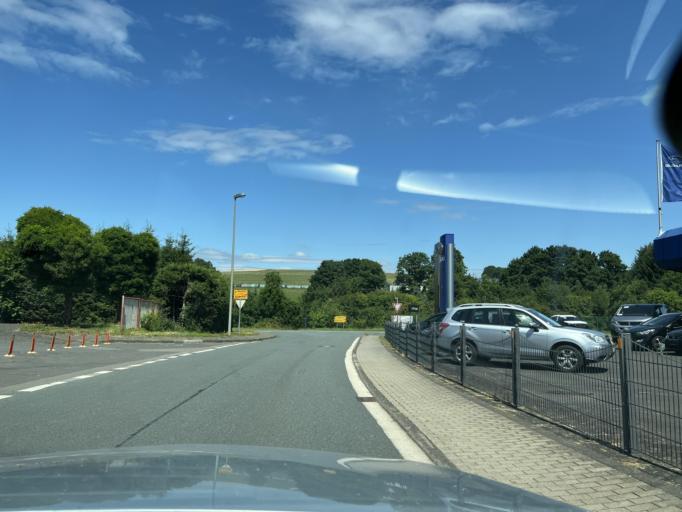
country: DE
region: North Rhine-Westphalia
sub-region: Regierungsbezirk Arnsberg
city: Wenden
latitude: 50.9668
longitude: 7.8994
